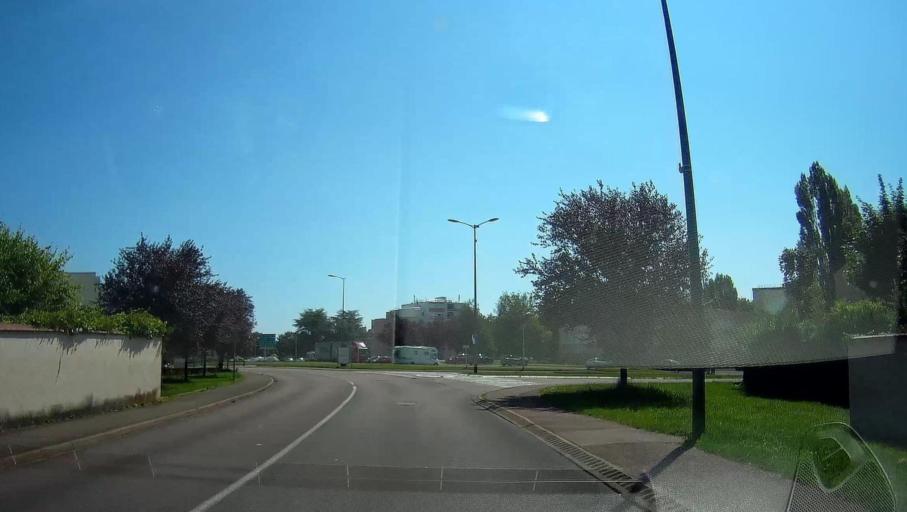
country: FR
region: Bourgogne
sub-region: Departement de la Cote-d'Or
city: Beaune
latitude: 47.0182
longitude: 4.8328
